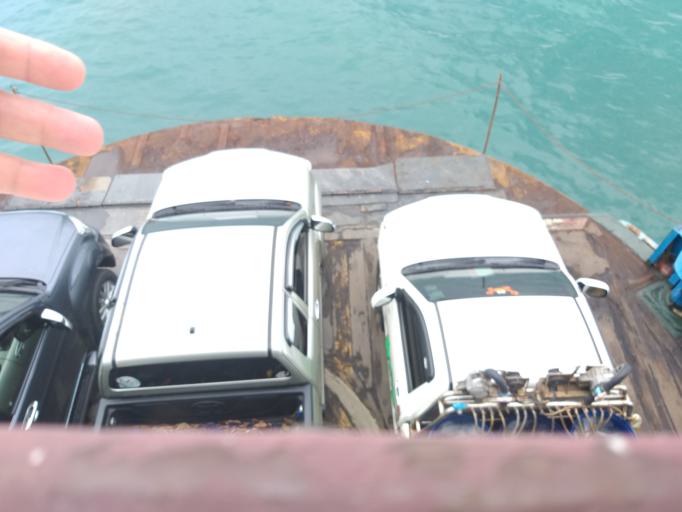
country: TH
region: Trat
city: Laem Ngop
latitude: 12.1704
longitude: 102.2969
